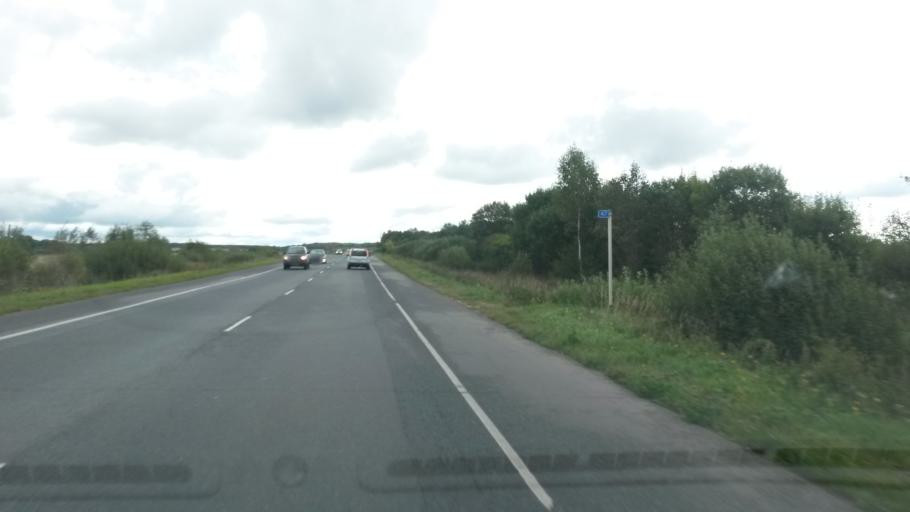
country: RU
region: Ivanovo
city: Rodniki
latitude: 57.0877
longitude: 41.6401
